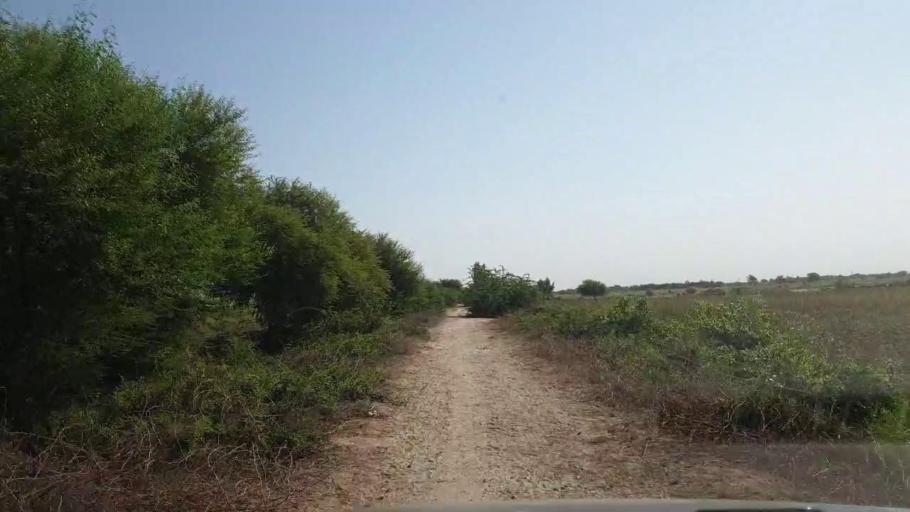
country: PK
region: Sindh
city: Kadhan
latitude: 24.5944
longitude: 69.0063
